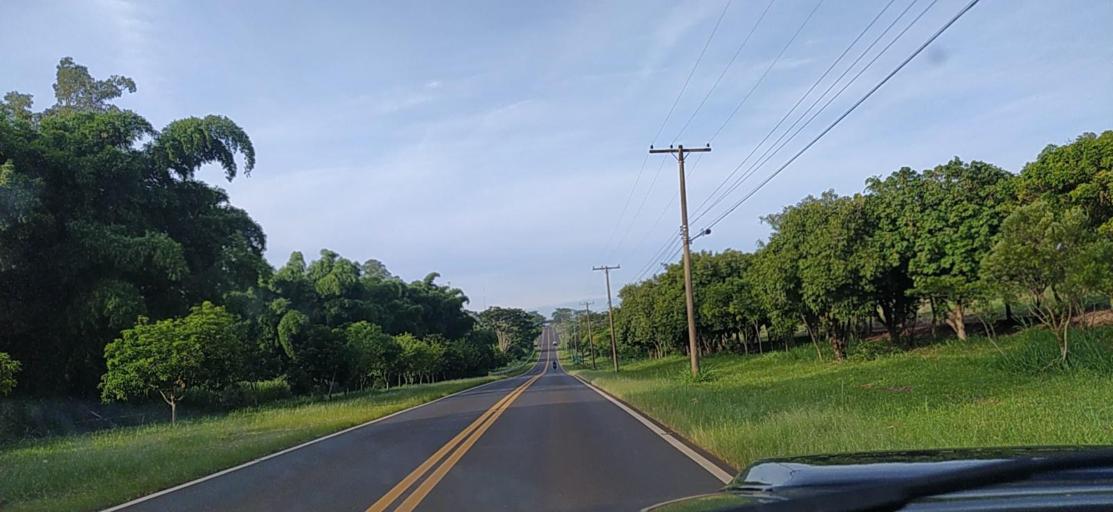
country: BR
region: Sao Paulo
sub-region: Pindorama
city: Pindorama
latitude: -21.2025
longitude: -48.9265
